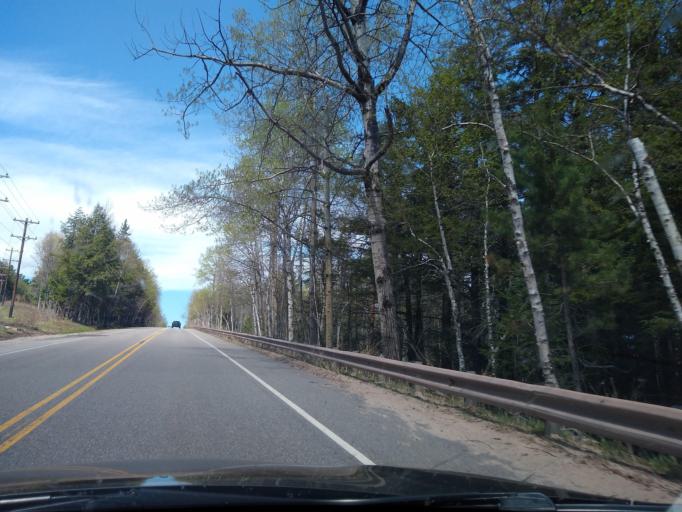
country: US
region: Michigan
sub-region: Marquette County
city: Trowbridge Park
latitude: 46.6191
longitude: -87.4666
